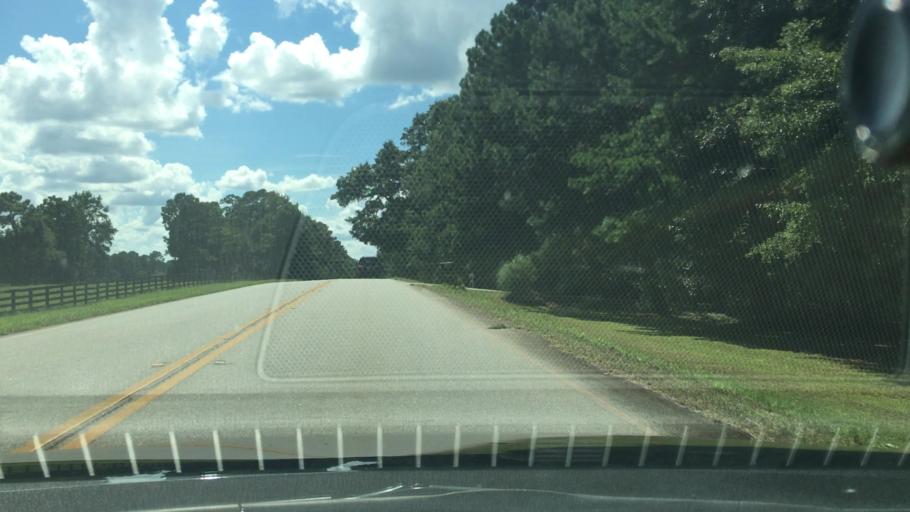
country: US
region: Georgia
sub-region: Jasper County
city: Monticello
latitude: 33.3038
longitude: -83.6237
